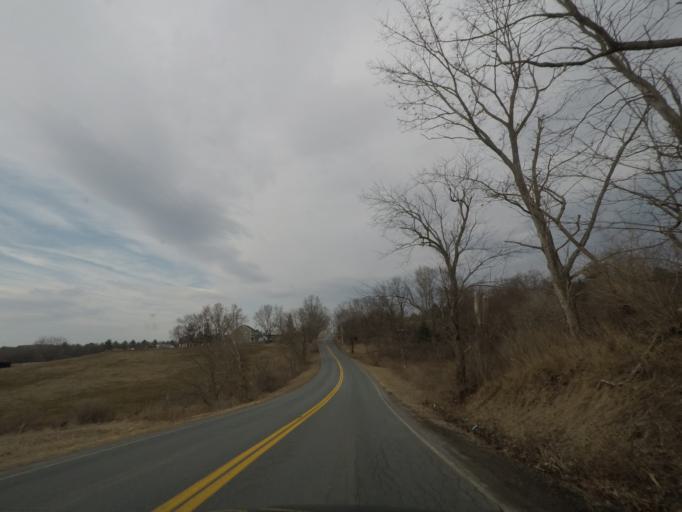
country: US
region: New York
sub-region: Washington County
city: Cambridge
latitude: 42.9413
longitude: -73.4899
